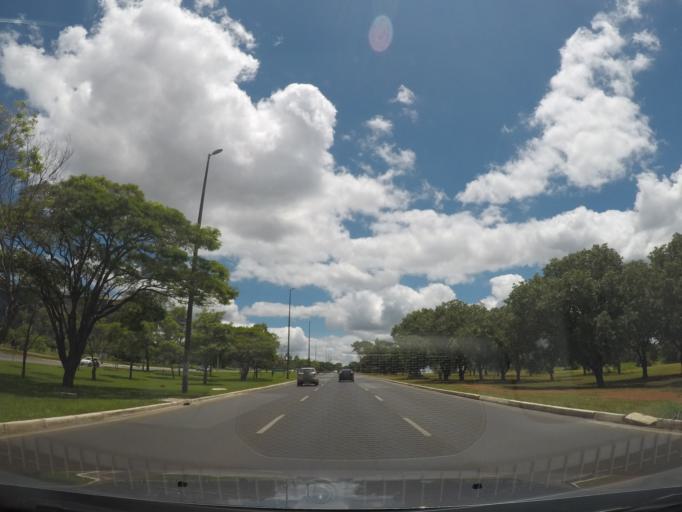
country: BR
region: Federal District
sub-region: Brasilia
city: Brasilia
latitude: -15.8144
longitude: -47.8695
